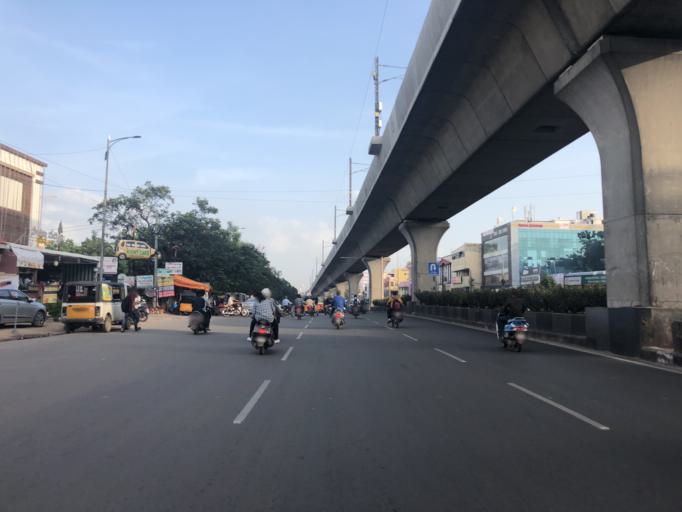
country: IN
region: Telangana
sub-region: Rangareddi
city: Kukatpalli
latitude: 17.4544
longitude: 78.4348
